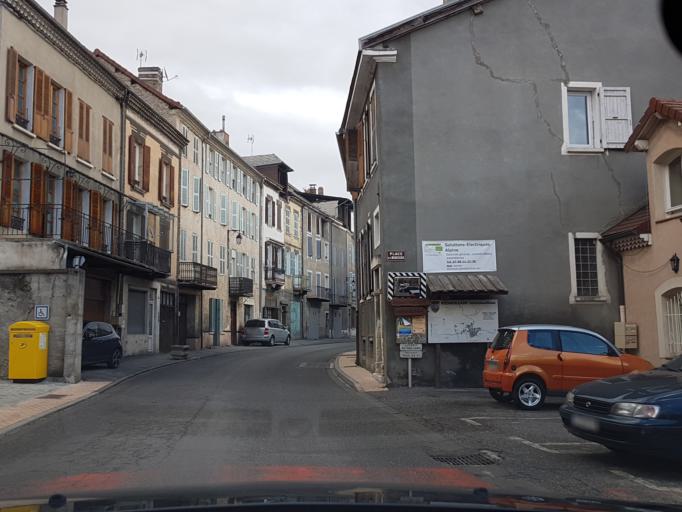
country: FR
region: Provence-Alpes-Cote d'Azur
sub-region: Departement des Hautes-Alpes
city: La Batie-Neuve
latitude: 44.4680
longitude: 6.1685
